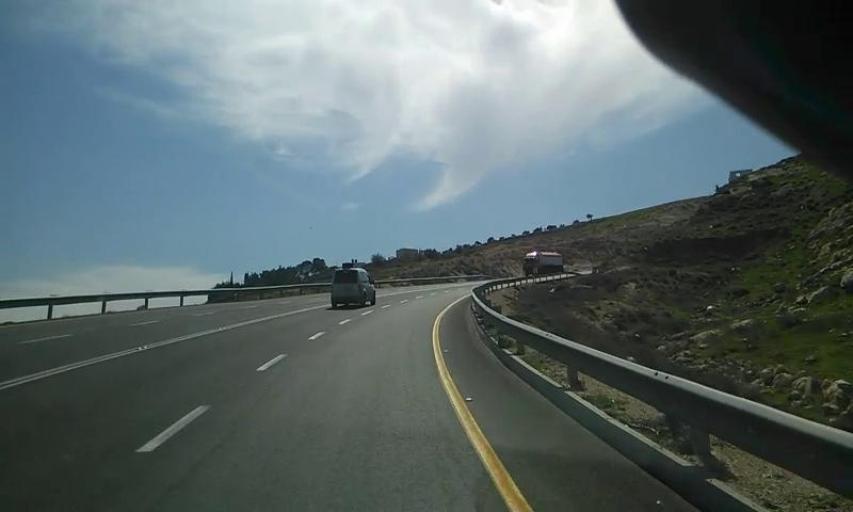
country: PS
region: West Bank
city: Bayt Ta`mar
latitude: 31.6741
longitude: 35.2443
